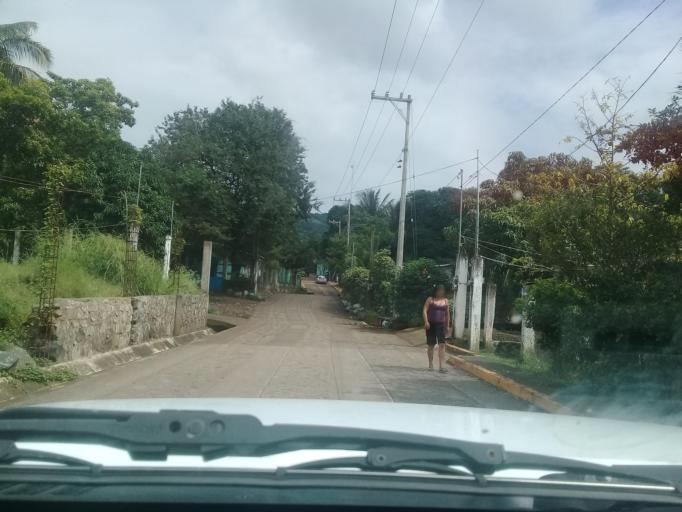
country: MX
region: Veracruz
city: Comoapan
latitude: 18.4095
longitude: -95.1596
